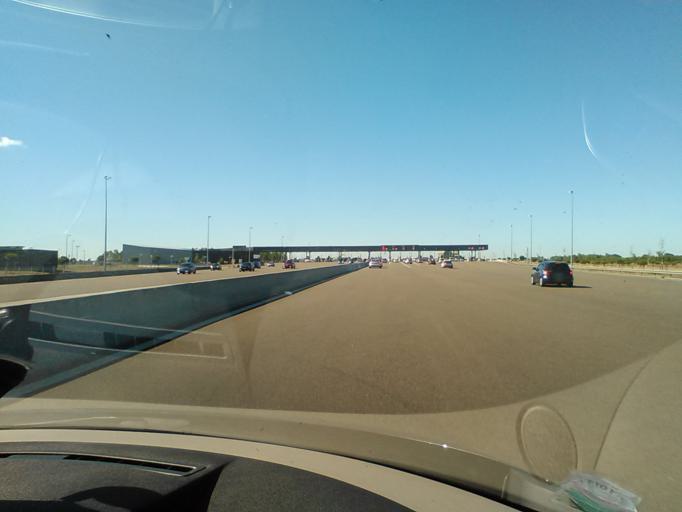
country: FR
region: Aquitaine
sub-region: Departement des Landes
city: Pissos
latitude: 44.3494
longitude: -0.8588
